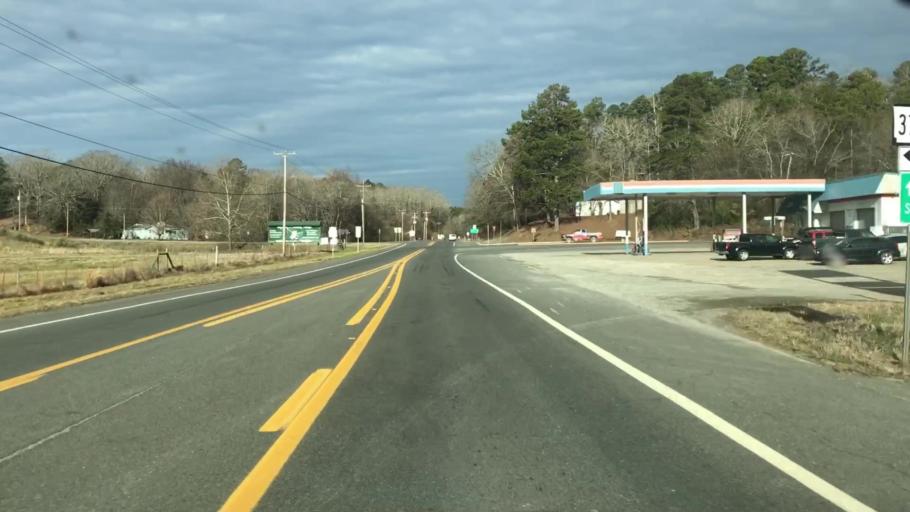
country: US
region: Arkansas
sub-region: Montgomery County
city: Mount Ida
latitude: 34.5618
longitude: -93.6388
